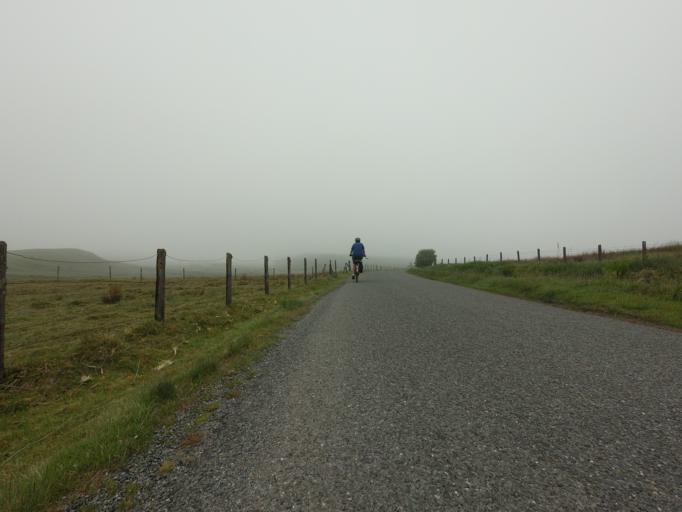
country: GB
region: Scotland
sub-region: Perth and Kinross
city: Kinross
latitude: 56.1529
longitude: -3.4535
